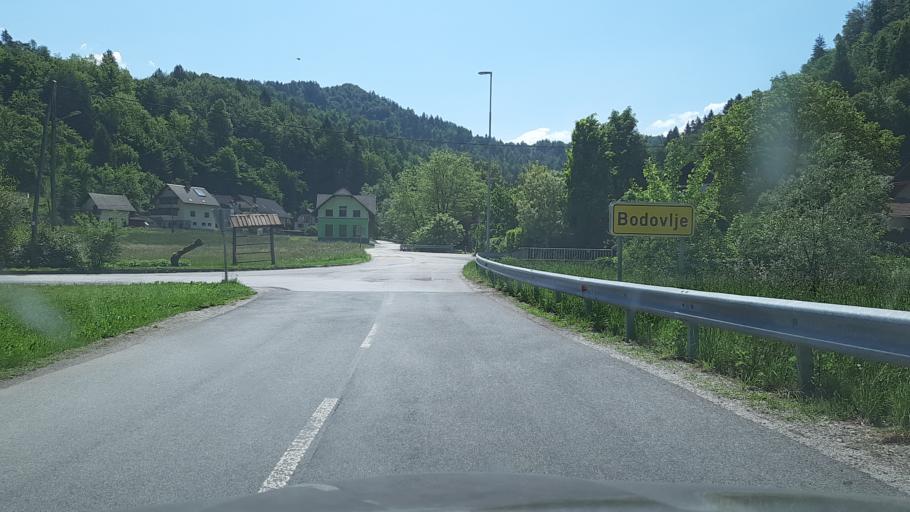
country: SI
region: Skofja Loka
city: Skofja Loka
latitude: 46.1505
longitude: 14.2913
